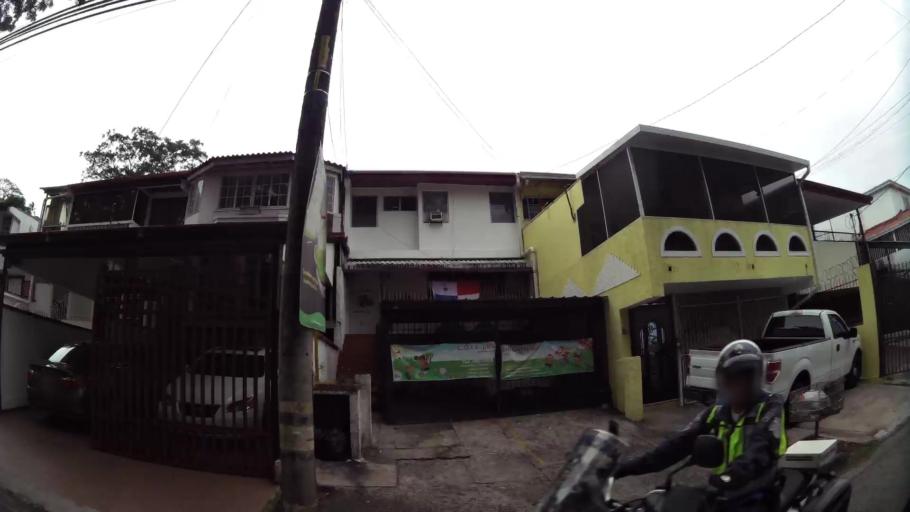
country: PA
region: Panama
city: Panama
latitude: 9.0182
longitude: -79.5249
